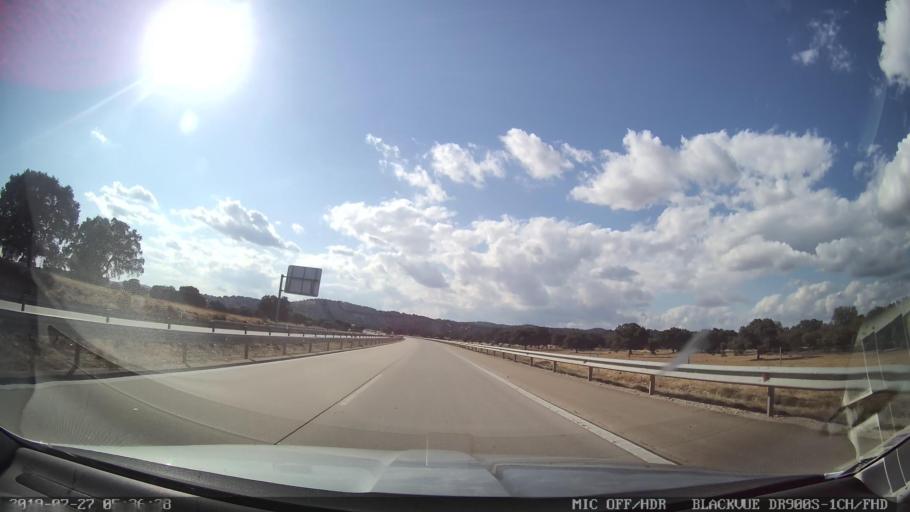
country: ES
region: Castille-La Mancha
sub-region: Province of Toledo
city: Cervera de los Montes
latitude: 40.0166
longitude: -4.7871
